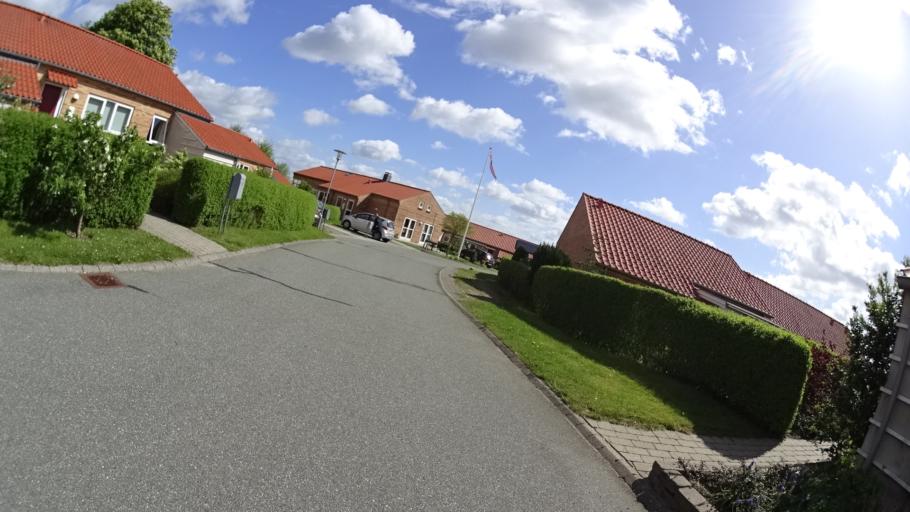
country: DK
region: Central Jutland
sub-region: Arhus Kommune
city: Stavtrup
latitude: 56.1267
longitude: 10.1149
